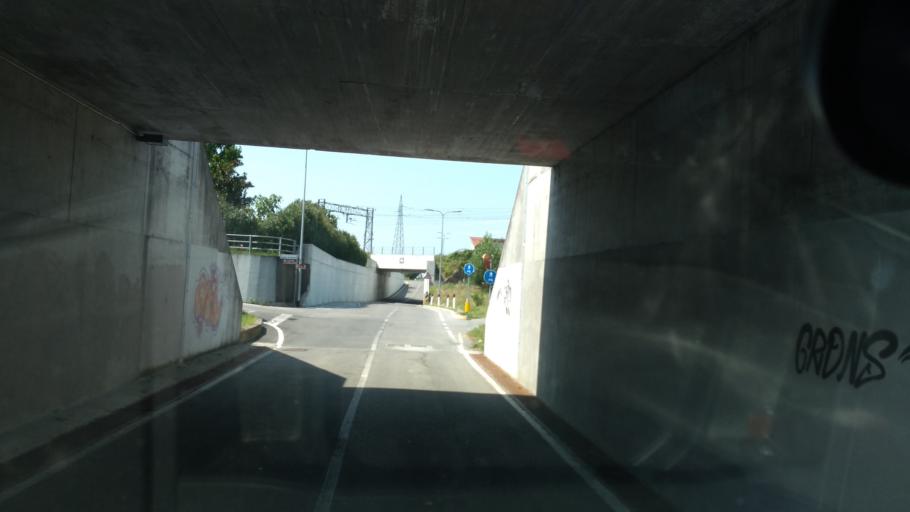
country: IT
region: Lombardy
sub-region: Provincia di Bergamo
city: Treviglio
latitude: 45.5178
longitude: 9.5793
